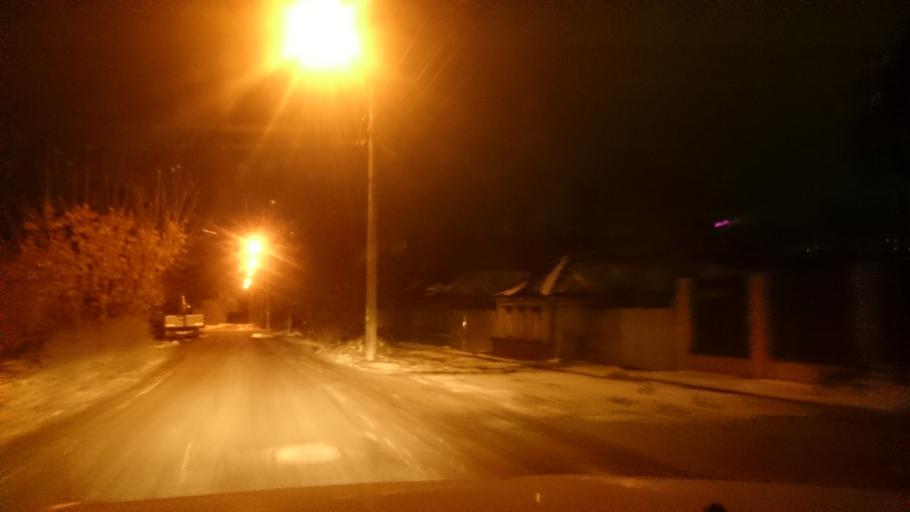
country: RU
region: Tula
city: Tula
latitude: 54.1859
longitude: 37.6332
